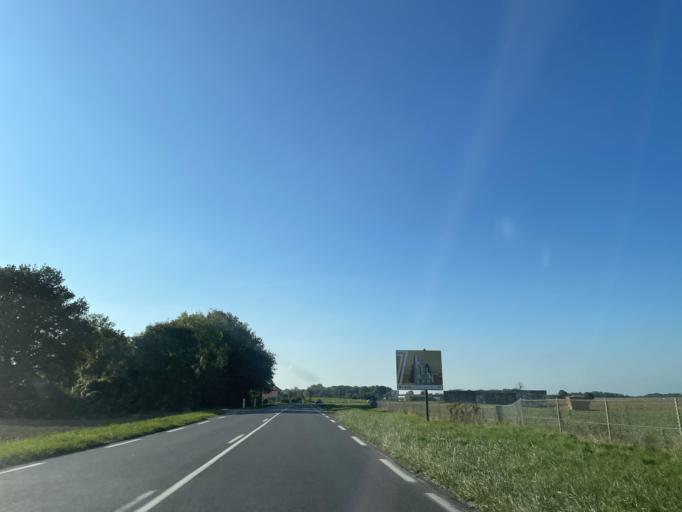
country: FR
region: Ile-de-France
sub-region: Departement de Seine-et-Marne
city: Pommeuse
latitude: 48.8350
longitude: 2.9926
